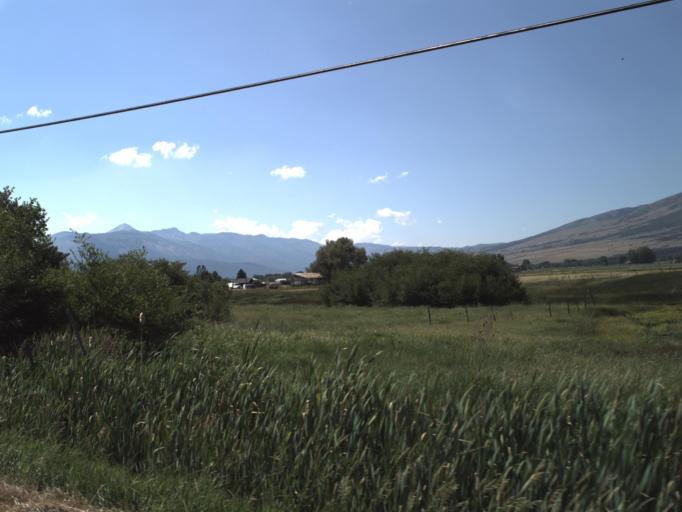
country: US
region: Utah
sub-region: Weber County
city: Wolf Creek
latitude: 41.2622
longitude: -111.7511
